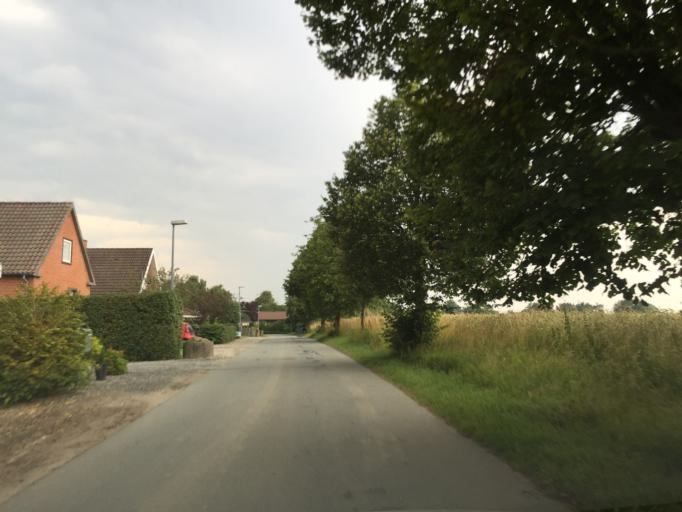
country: DK
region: Central Jutland
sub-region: Viborg Kommune
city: Bjerringbro
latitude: 56.3353
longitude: 9.6415
